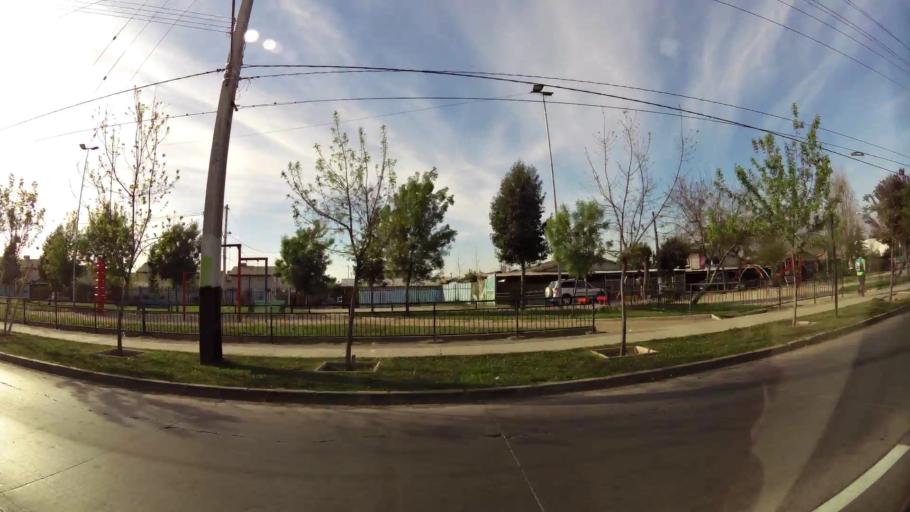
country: CL
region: Santiago Metropolitan
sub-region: Provincia de Cordillera
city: Puente Alto
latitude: -33.6144
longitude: -70.5924
